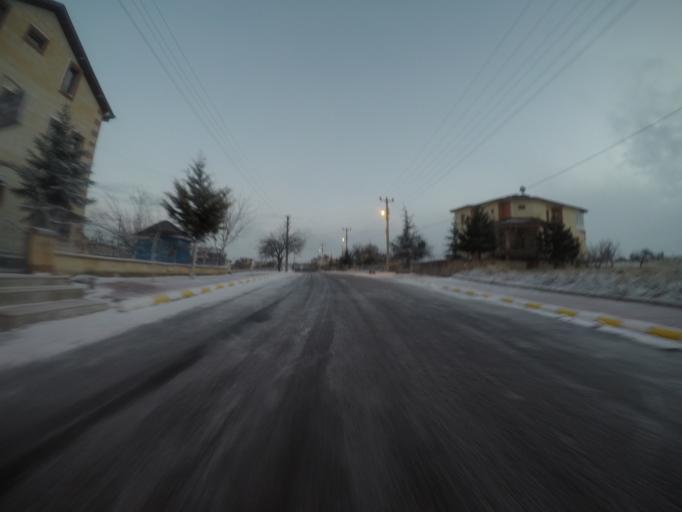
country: TR
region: Nevsehir
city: Goereme
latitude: 38.6232
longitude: 34.7986
